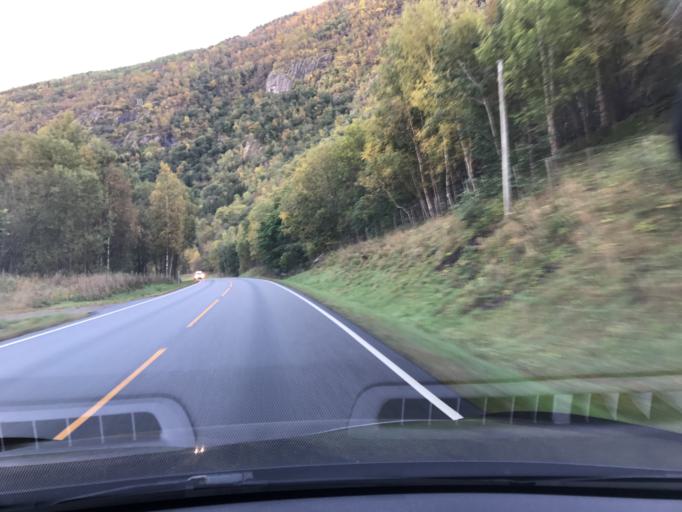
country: NO
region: Sogn og Fjordane
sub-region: Laerdal
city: Laerdalsoyri
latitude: 61.0963
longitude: 7.4786
